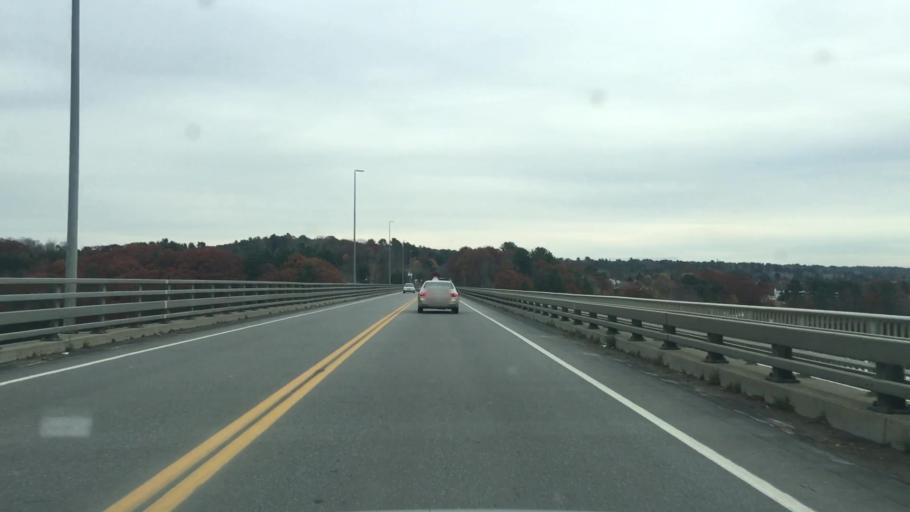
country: US
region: Maine
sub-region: Waldo County
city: Belfast
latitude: 44.4330
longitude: -69.0116
